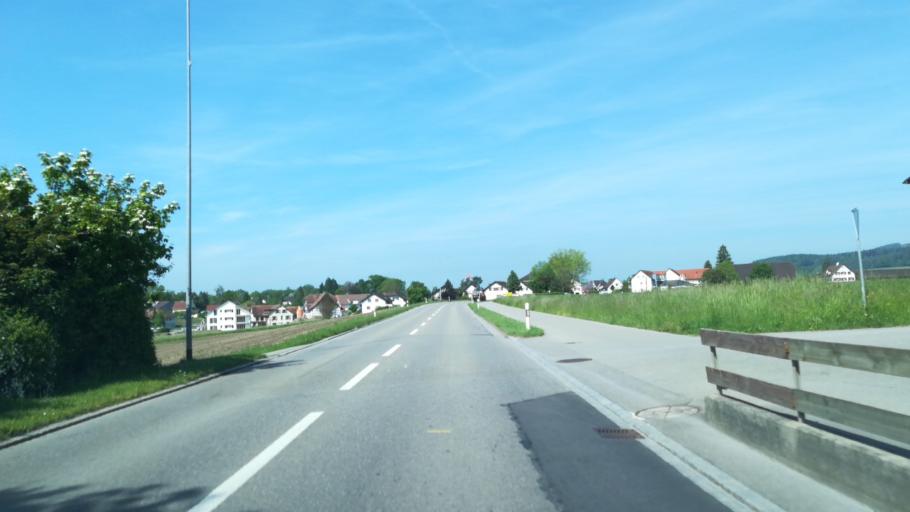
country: CH
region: Thurgau
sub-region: Frauenfeld District
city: Pfyn
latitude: 47.5966
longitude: 8.9629
